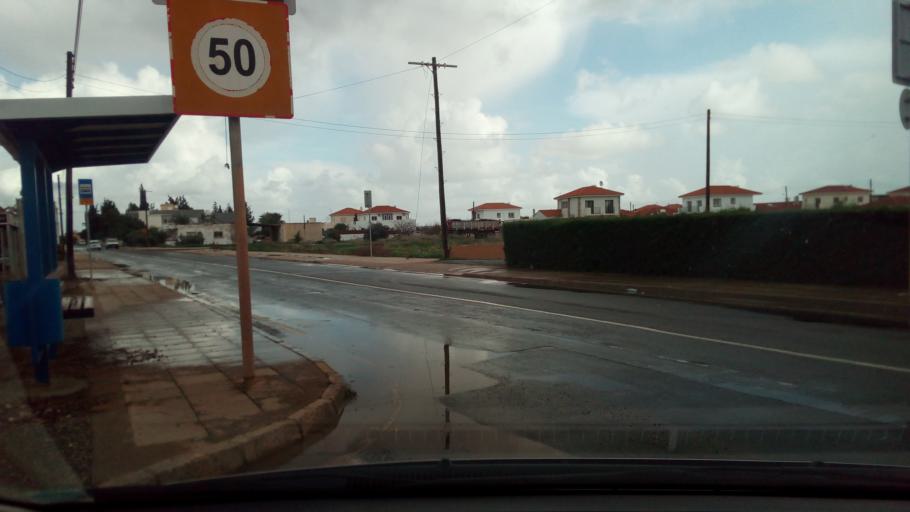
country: CY
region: Ammochostos
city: Liopetri
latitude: 35.0118
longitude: 33.8971
